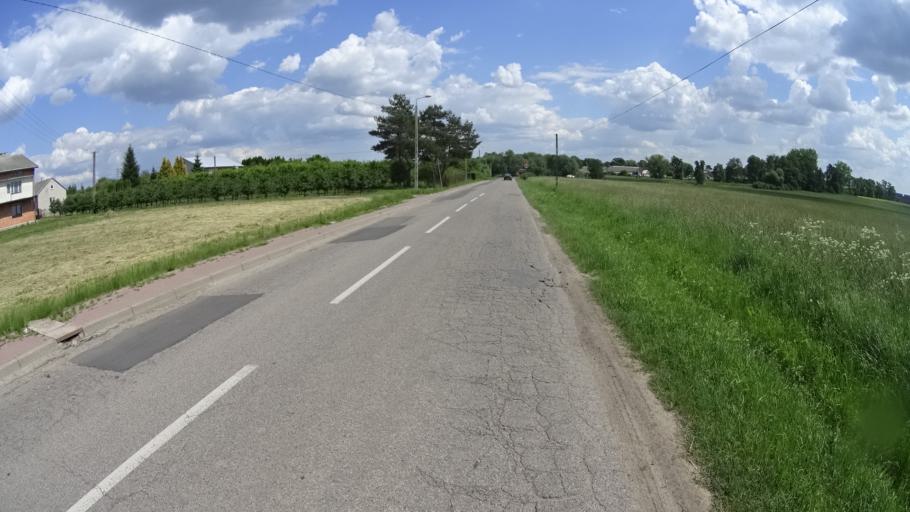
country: PL
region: Masovian Voivodeship
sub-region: Powiat piaseczynski
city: Tarczyn
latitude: 52.0364
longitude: 20.8219
